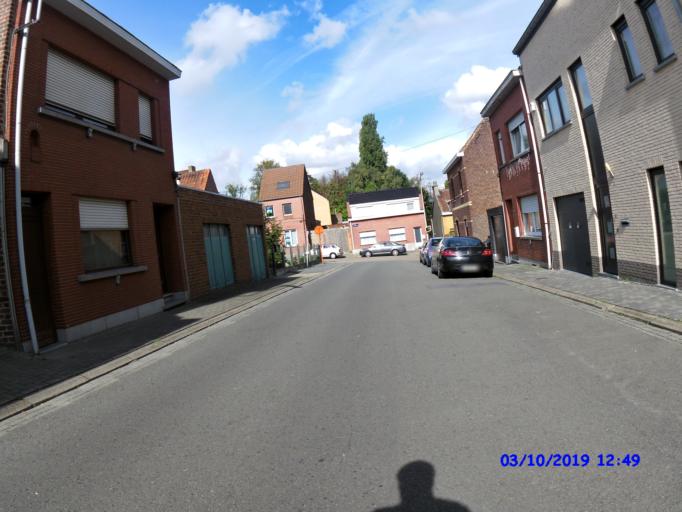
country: BE
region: Flanders
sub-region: Provincie Oost-Vlaanderen
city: Denderleeuw
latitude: 50.8846
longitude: 4.0816
